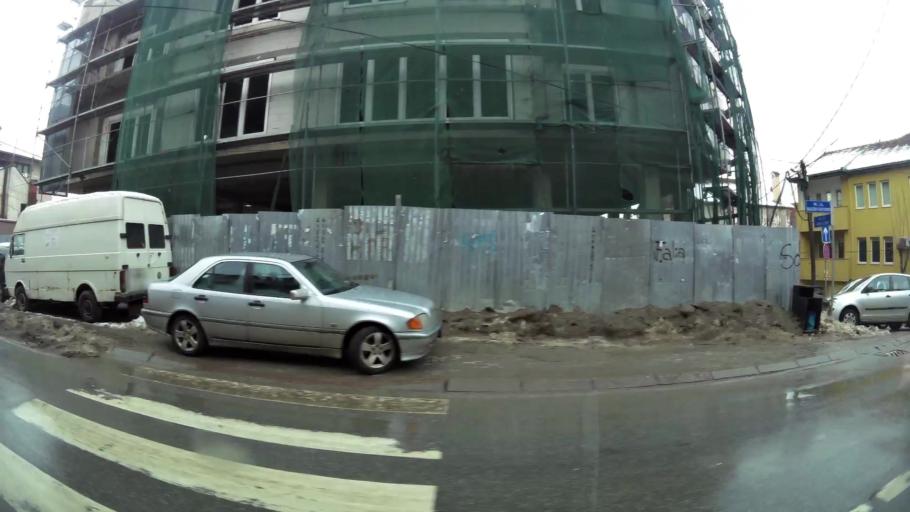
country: XK
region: Pristina
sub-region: Komuna e Prishtines
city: Pristina
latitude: 42.6672
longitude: 21.1730
